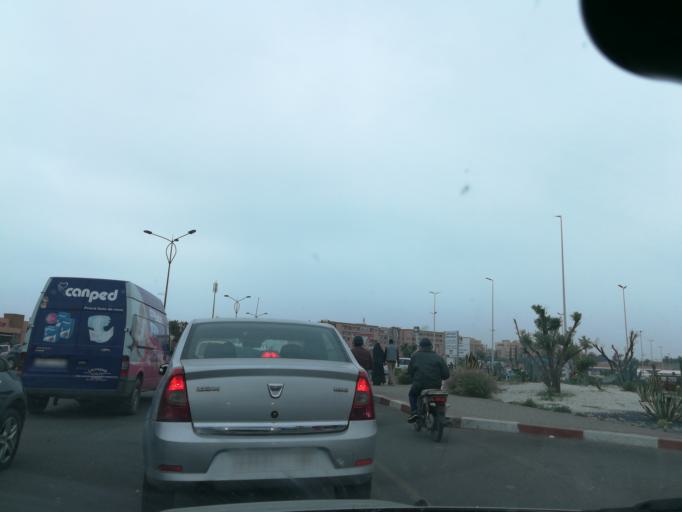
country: MA
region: Marrakech-Tensift-Al Haouz
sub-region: Marrakech
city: Marrakesh
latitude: 31.6691
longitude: -8.0124
